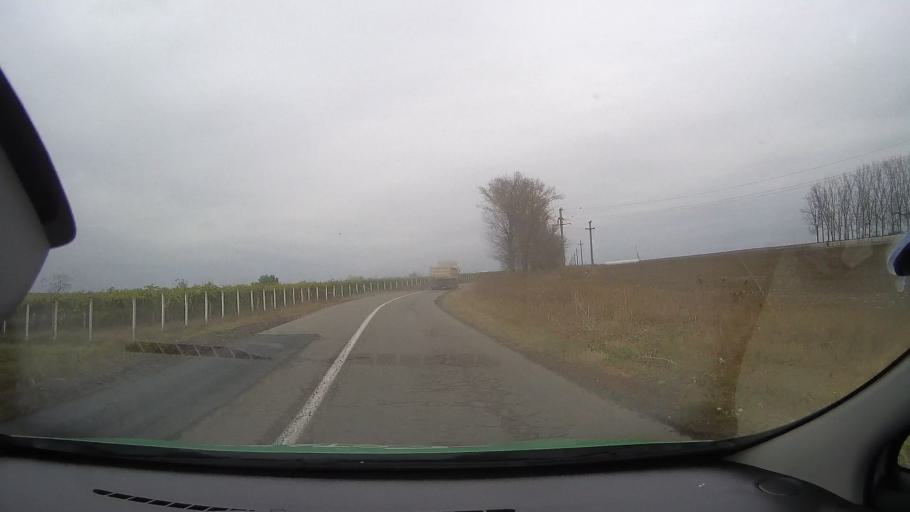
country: RO
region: Constanta
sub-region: Comuna Mihail Kogalniceanu
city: Mihail Kogalniceanu
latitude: 44.3824
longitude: 28.4616
